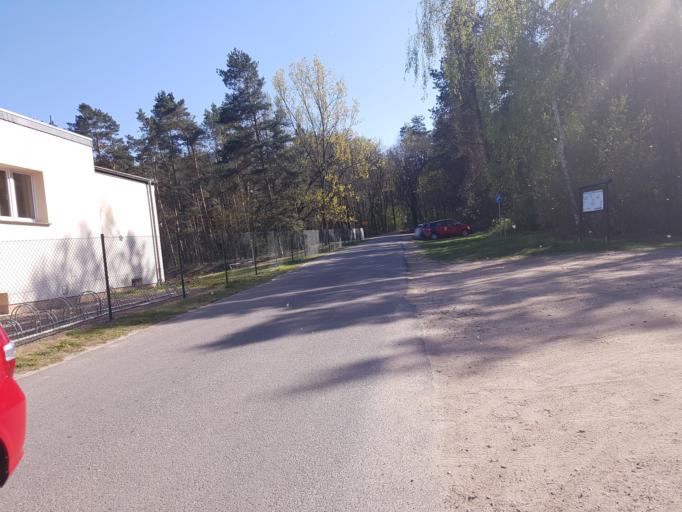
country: DE
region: Brandenburg
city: Groden
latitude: 51.3997
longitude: 13.5644
